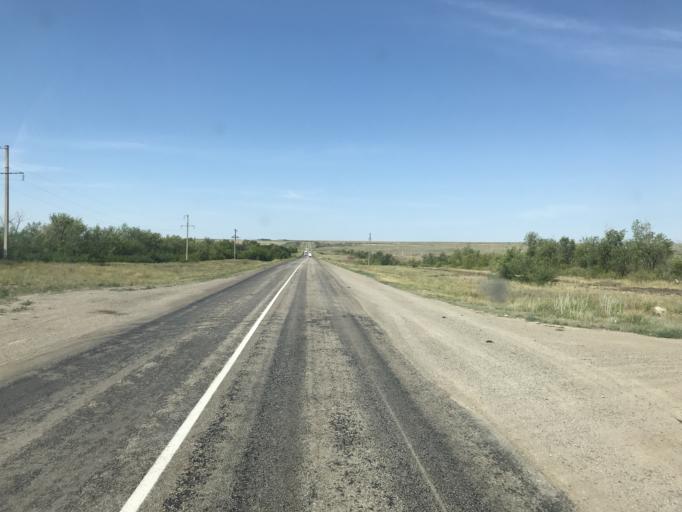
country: KZ
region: Aqtoebe
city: Martuk
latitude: 50.2360
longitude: 56.6713
